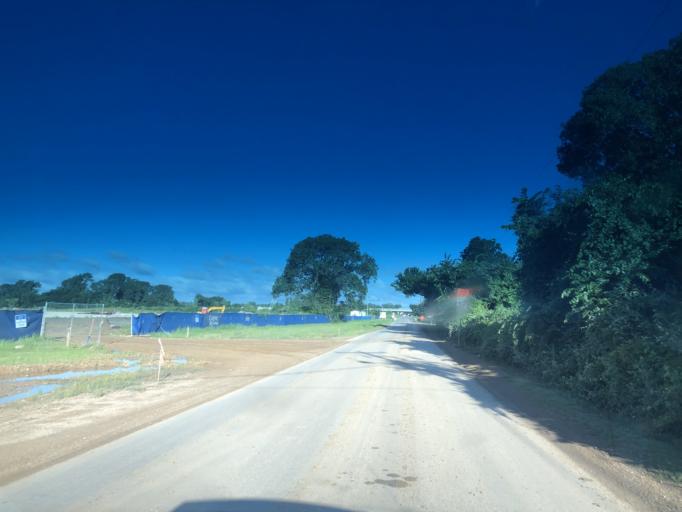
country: US
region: Texas
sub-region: Dallas County
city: Grand Prairie
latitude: 32.7924
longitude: -97.0117
